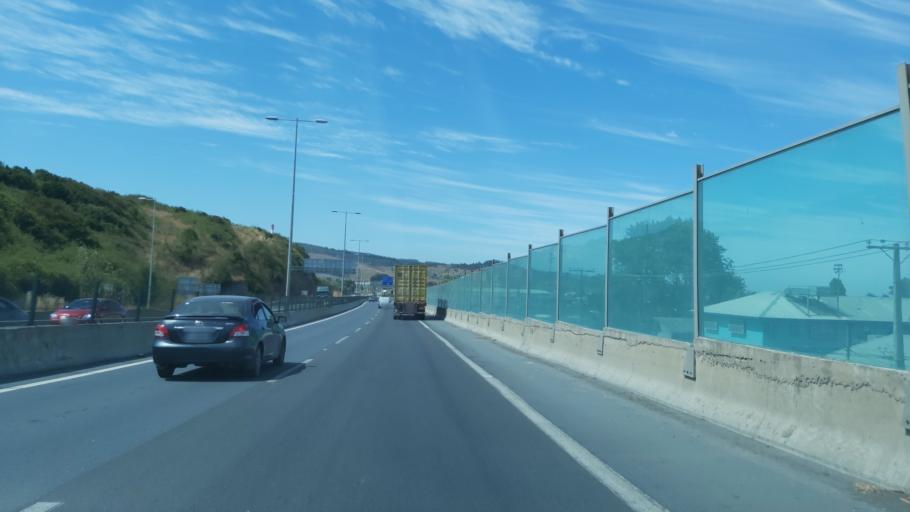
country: CL
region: Biobio
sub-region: Provincia de Concepcion
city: Coronel
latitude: -37.0282
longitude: -73.1352
